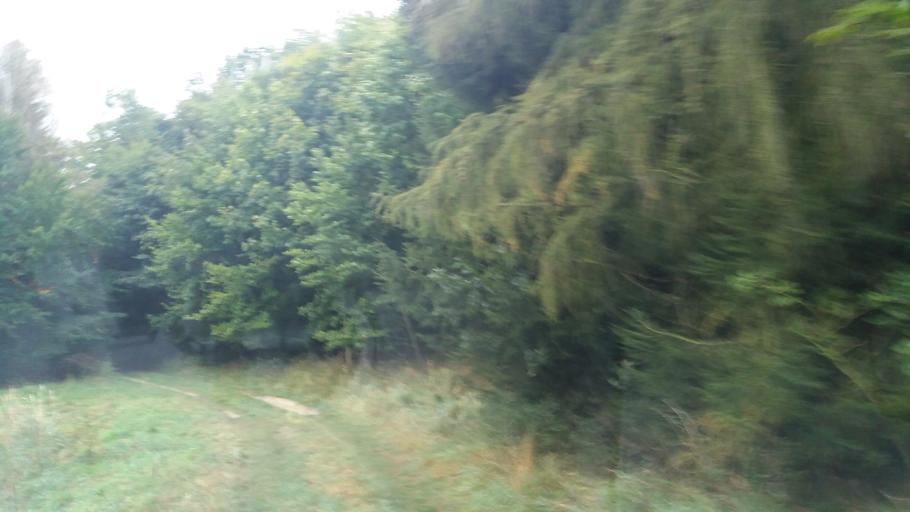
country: PL
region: West Pomeranian Voivodeship
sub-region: Powiat choszczenski
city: Pelczyce
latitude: 53.0691
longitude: 15.2809
